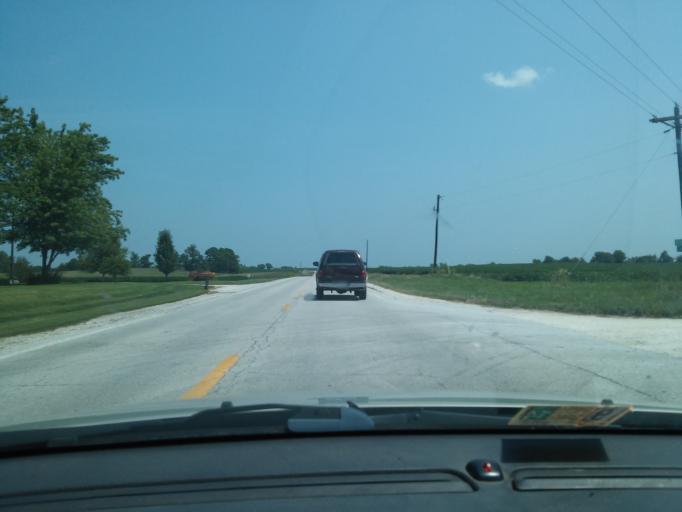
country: US
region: Illinois
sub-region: Pike County
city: Pittsfield
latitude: 39.5776
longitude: -90.9078
